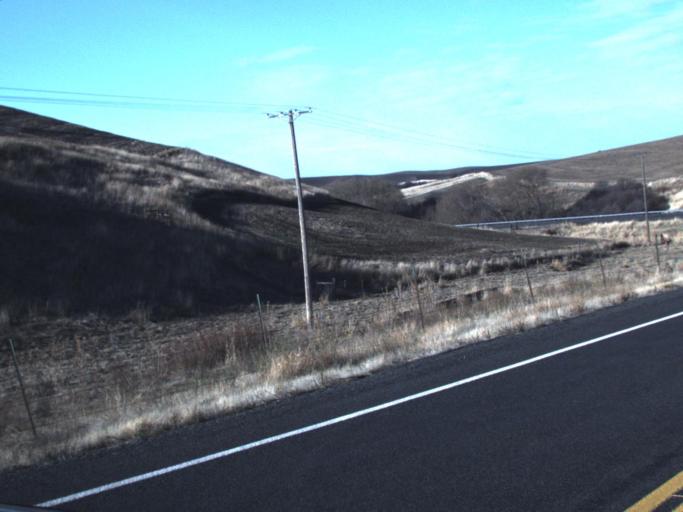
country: US
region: Washington
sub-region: Whitman County
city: Pullman
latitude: 46.7302
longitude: -117.3036
